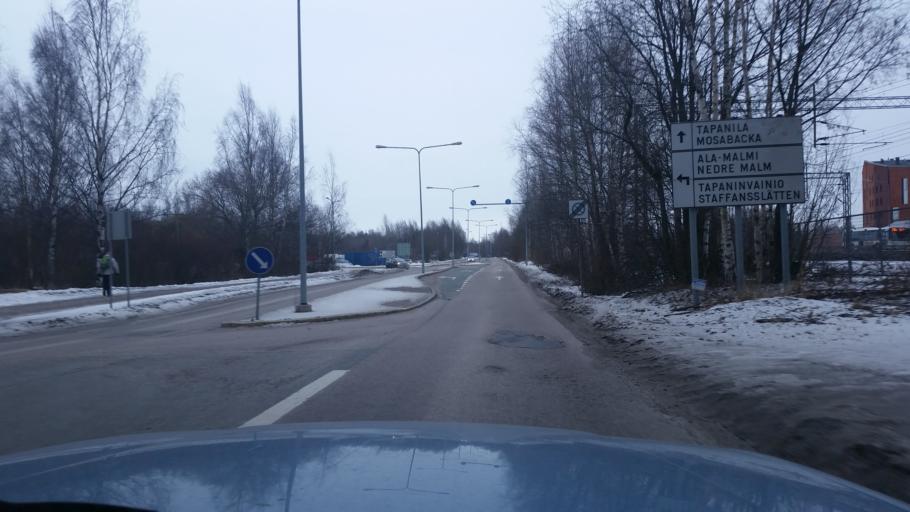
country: FI
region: Uusimaa
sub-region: Helsinki
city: Vantaa
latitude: 60.2546
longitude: 25.0159
